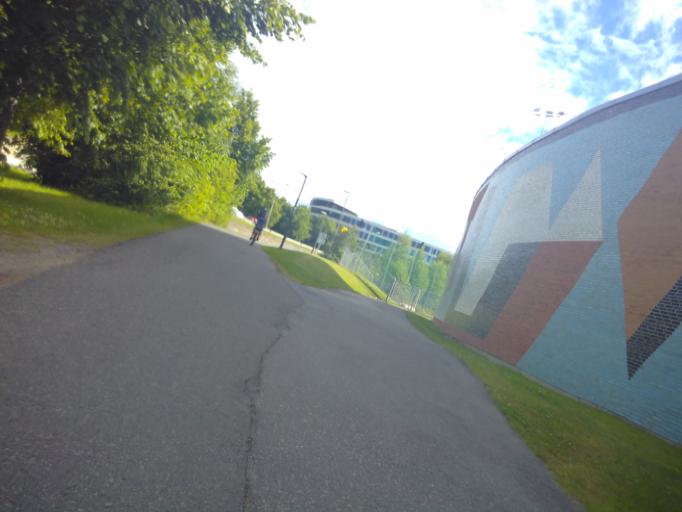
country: NO
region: Oslo
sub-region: Oslo
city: Oslo
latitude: 59.9466
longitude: 10.7230
